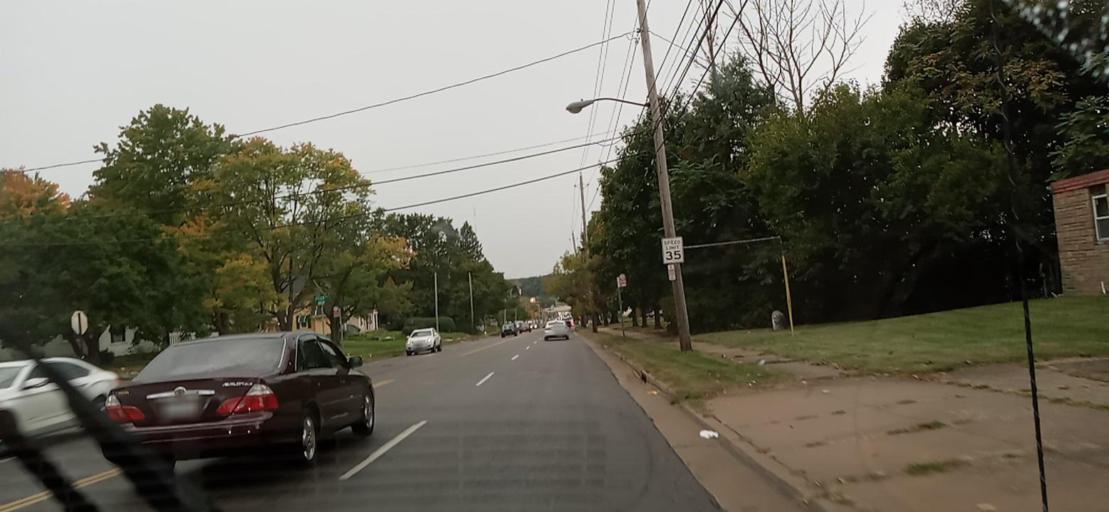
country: US
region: Ohio
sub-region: Summit County
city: Akron
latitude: 41.0667
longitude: -81.5631
